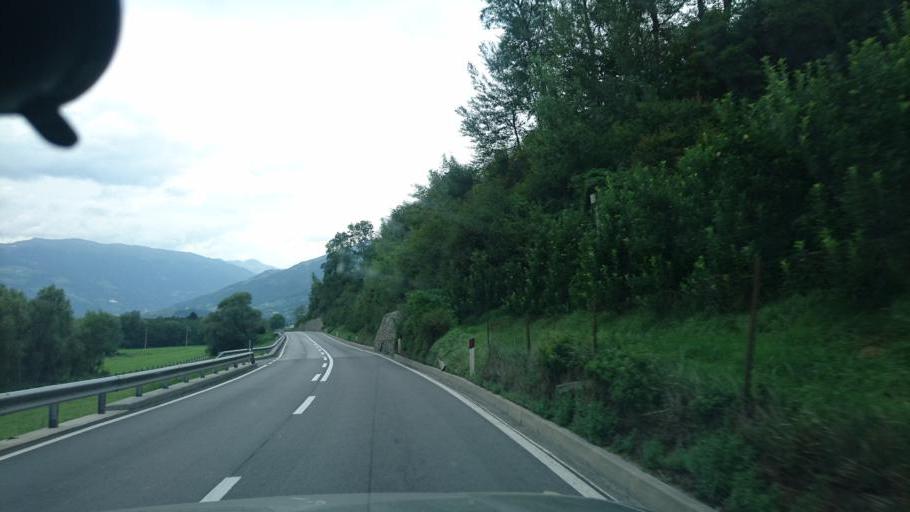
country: IT
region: Trentino-Alto Adige
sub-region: Bolzano
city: Sluderno
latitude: 46.6481
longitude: 10.5928
